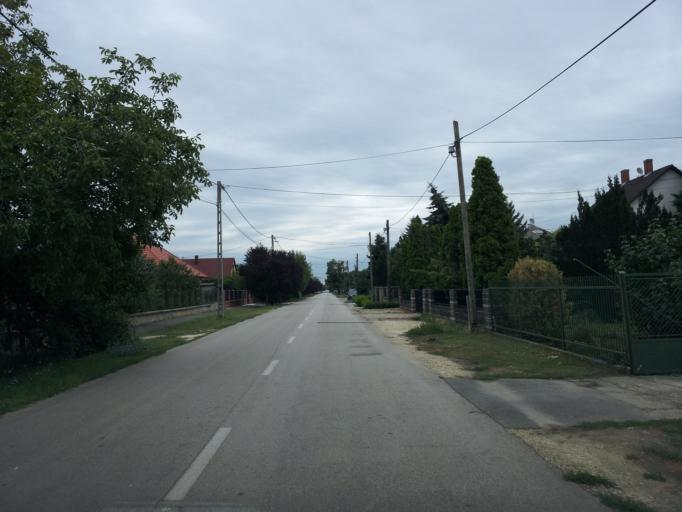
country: HU
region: Pest
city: Tarnok
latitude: 47.3716
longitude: 18.8686
